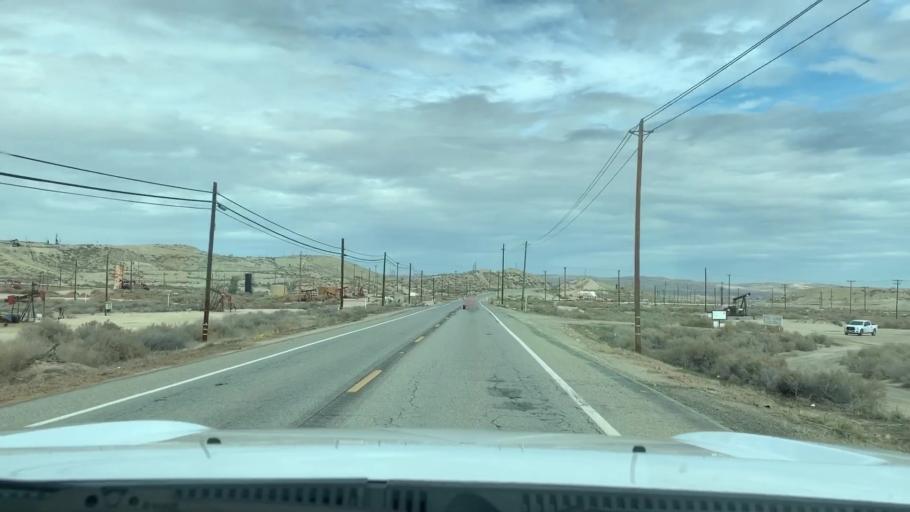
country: US
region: California
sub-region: Kern County
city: Maricopa
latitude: 35.0730
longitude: -119.4020
